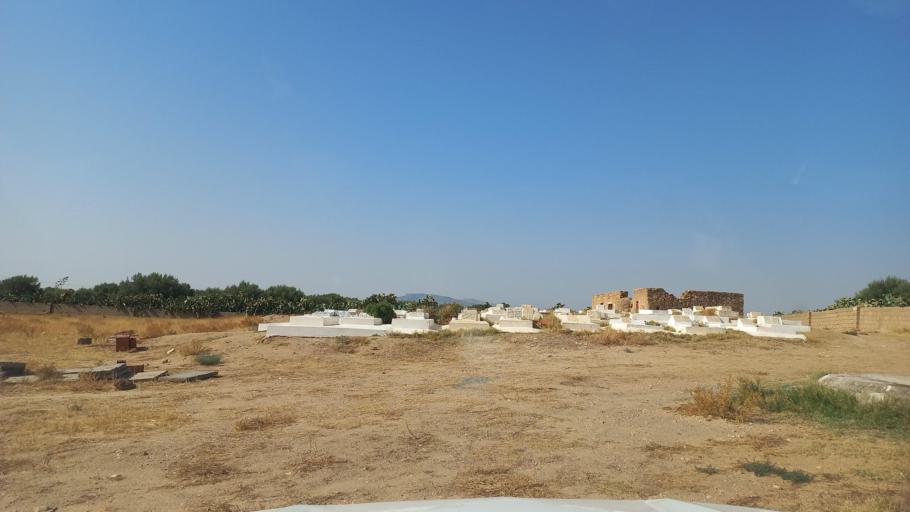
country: TN
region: Al Qasrayn
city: Kasserine
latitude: 35.2493
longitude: 9.0300
